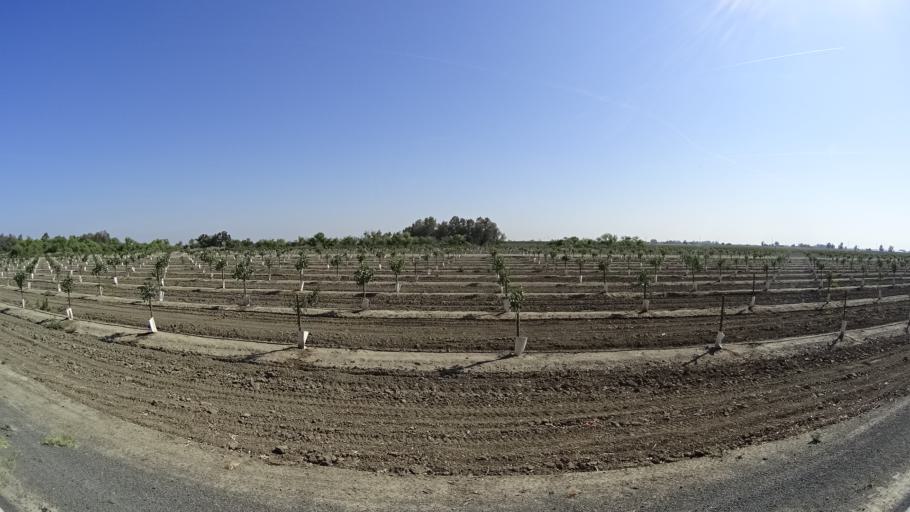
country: US
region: California
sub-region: Fresno County
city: Riverdale
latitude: 36.3612
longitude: -119.9133
